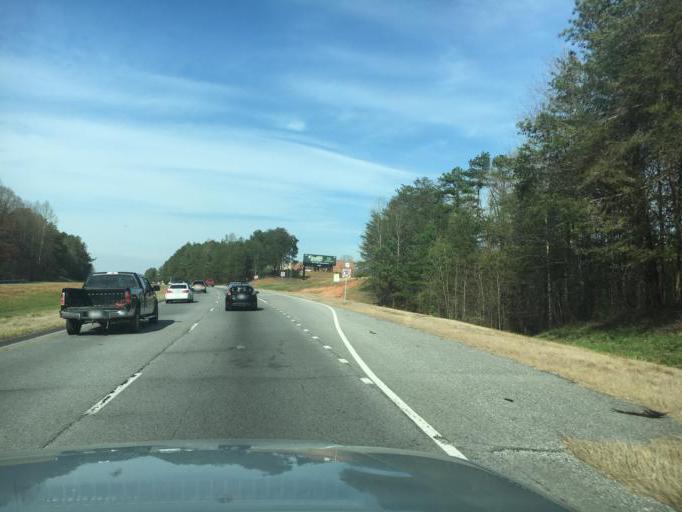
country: US
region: Georgia
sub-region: Hall County
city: Lula
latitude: 34.4162
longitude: -83.6565
